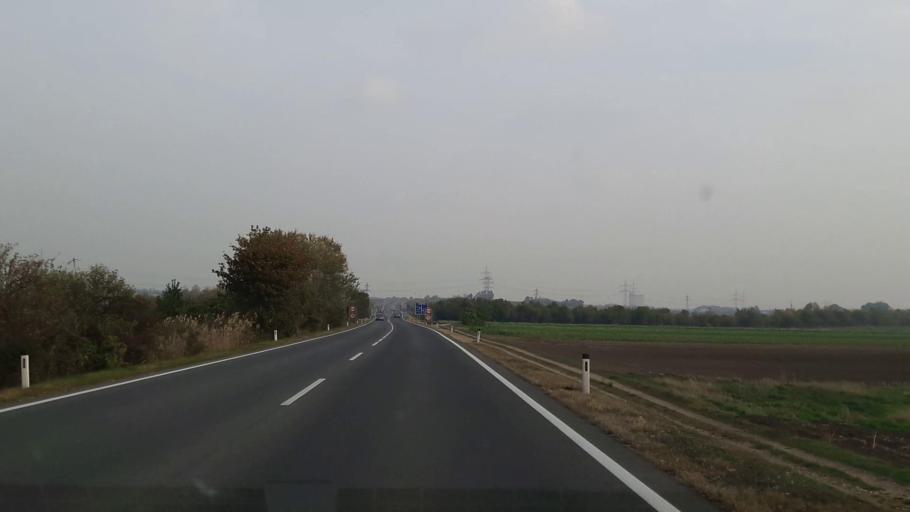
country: AT
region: Burgenland
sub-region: Politischer Bezirk Neusiedl am See
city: Parndorf
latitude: 48.0071
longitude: 16.8277
